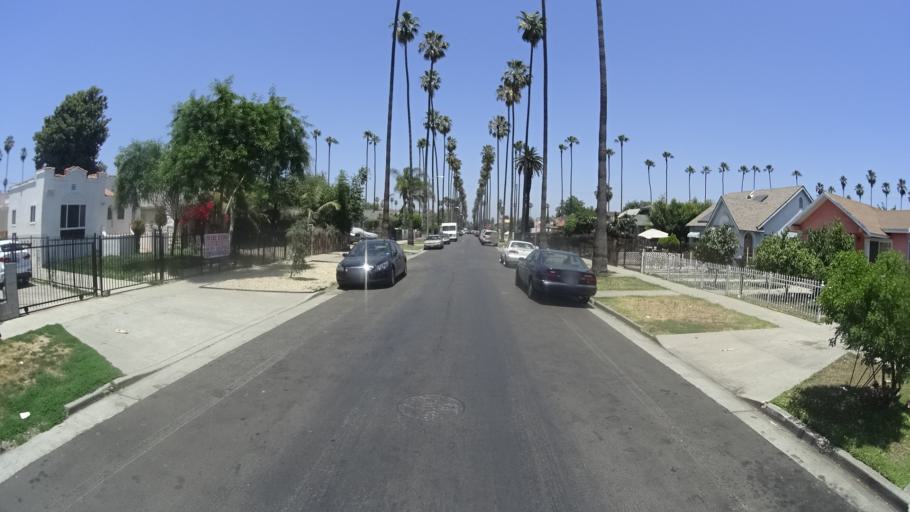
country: US
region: California
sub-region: Los Angeles County
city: View Park-Windsor Hills
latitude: 33.9900
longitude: -118.3126
